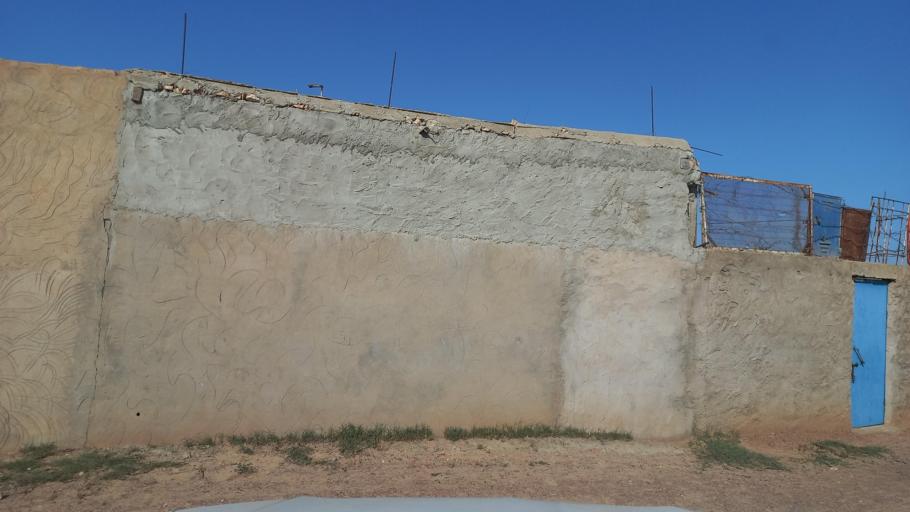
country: TN
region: Al Qasrayn
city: Kasserine
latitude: 35.3161
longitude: 9.0126
